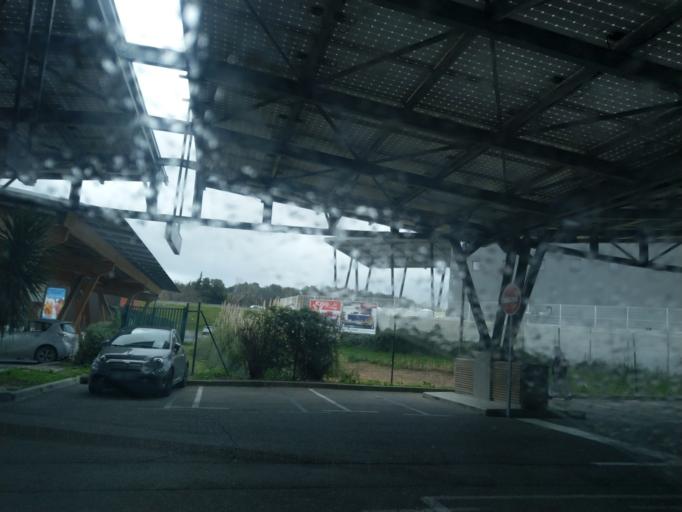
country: FR
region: Provence-Alpes-Cote d'Azur
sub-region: Departement des Bouches-du-Rhone
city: Septemes-les-Vallons
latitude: 43.4123
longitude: 5.3624
